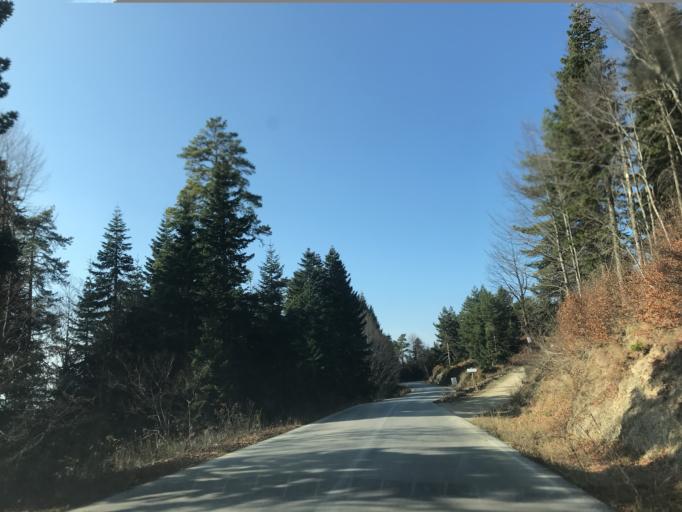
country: TR
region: Bolu
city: Bolu
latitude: 40.8884
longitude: 31.6784
